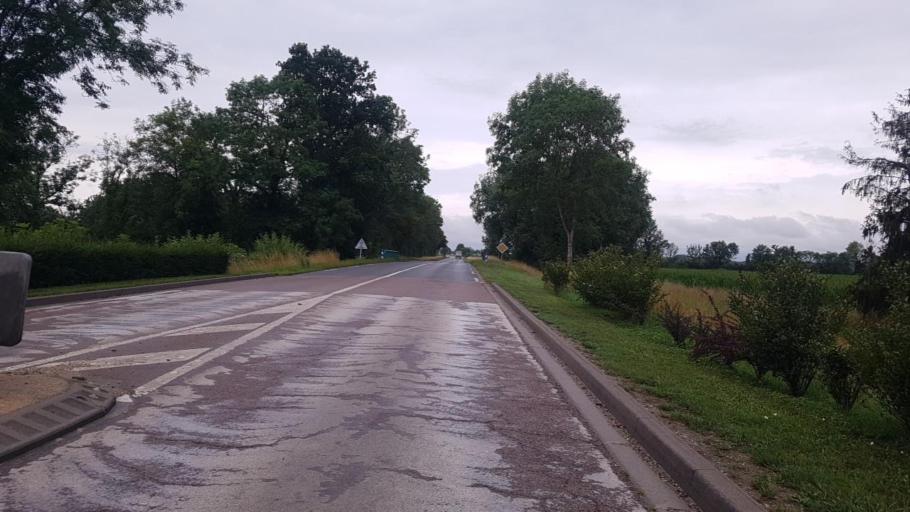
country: FR
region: Champagne-Ardenne
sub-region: Departement de la Marne
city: Vitry-le-Francois
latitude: 48.7415
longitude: 4.6230
